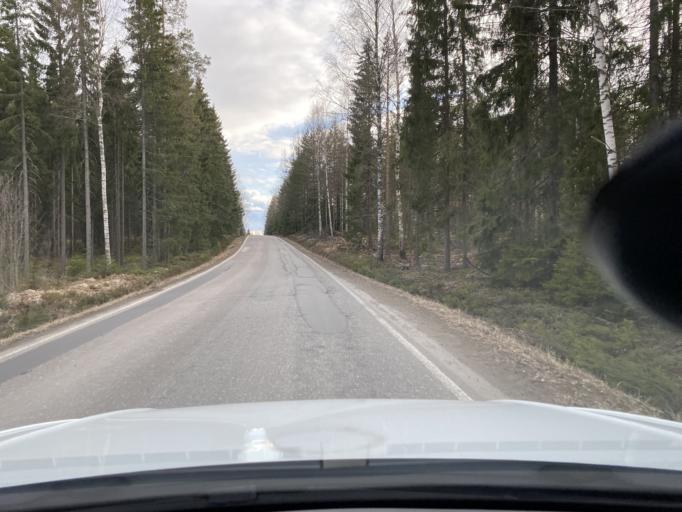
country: FI
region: Pirkanmaa
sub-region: Lounais-Pirkanmaa
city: Punkalaidun
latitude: 61.1334
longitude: 23.1508
